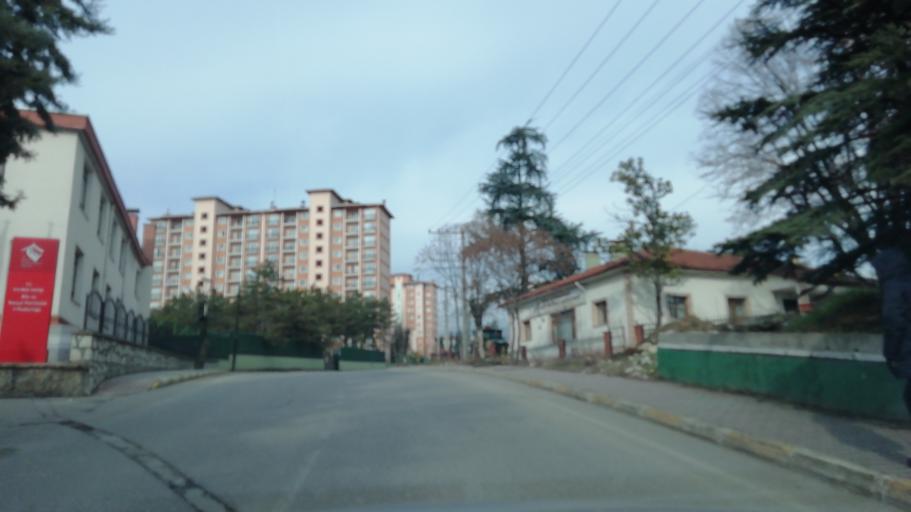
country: TR
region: Karabuk
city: Karabuk
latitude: 41.2007
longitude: 32.6266
